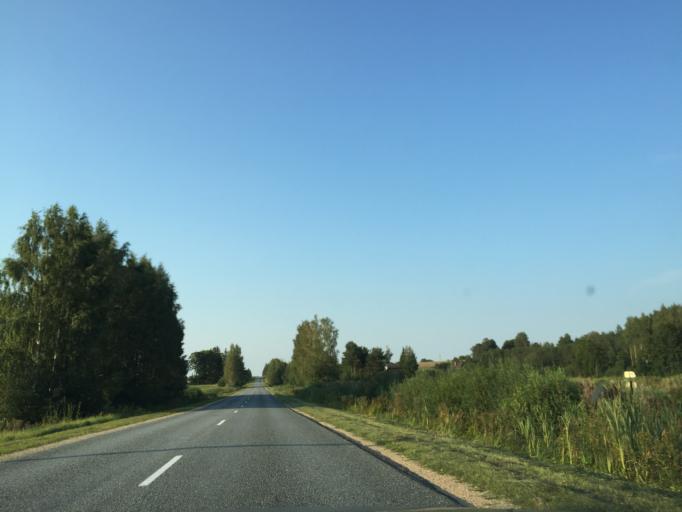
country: LV
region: Limbazu Rajons
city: Limbazi
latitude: 57.5636
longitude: 24.7666
